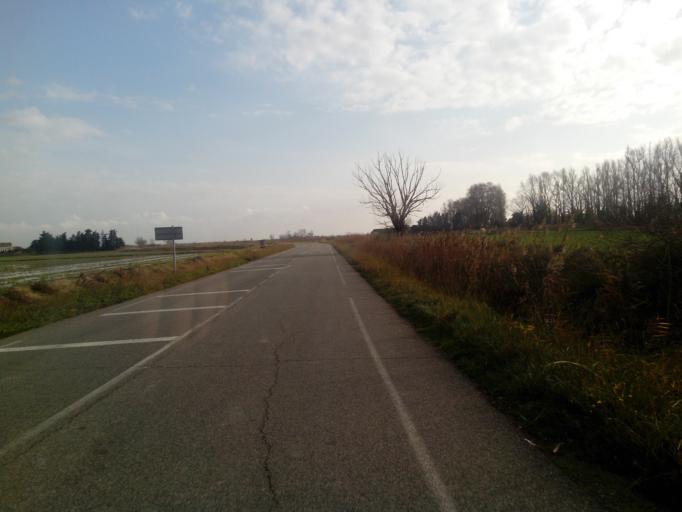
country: FR
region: Languedoc-Roussillon
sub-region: Departement du Gard
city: Saint-Gilles
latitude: 43.6082
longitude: 4.4784
